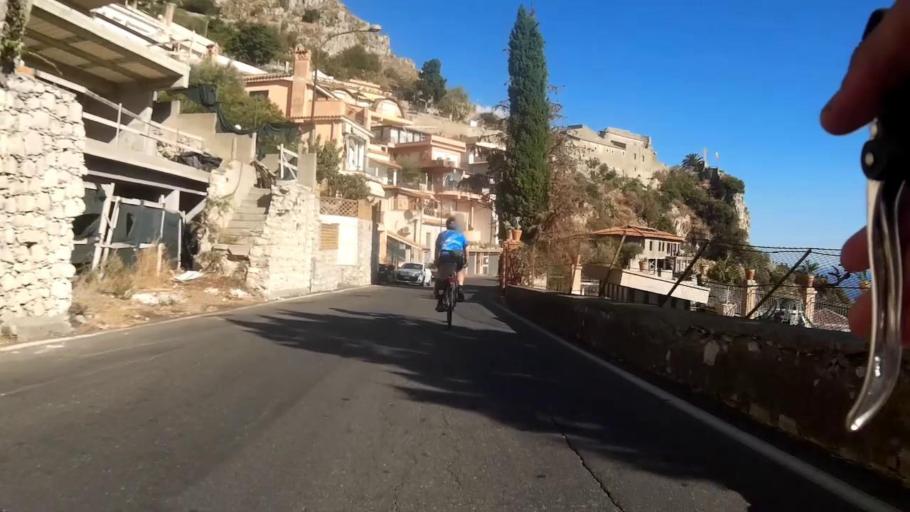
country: IT
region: Sicily
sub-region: Messina
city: Taormina
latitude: 37.8545
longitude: 15.2830
